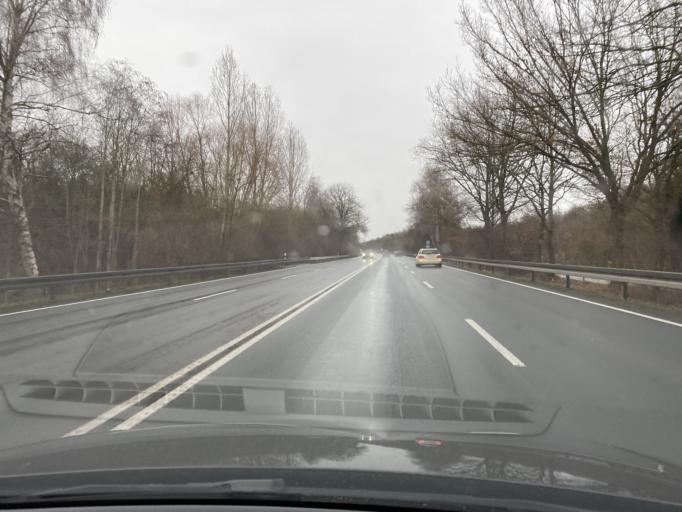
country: DE
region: North Rhine-Westphalia
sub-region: Regierungsbezirk Arnsberg
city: Lippstadt
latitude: 51.6925
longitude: 8.3631
